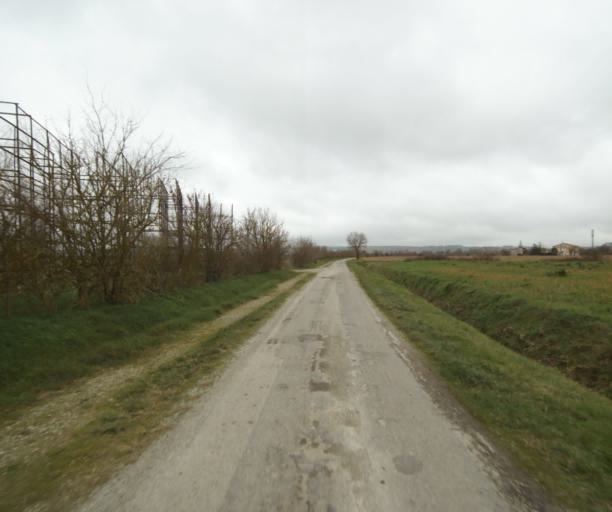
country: FR
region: Midi-Pyrenees
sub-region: Departement de l'Ariege
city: Mazeres
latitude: 43.2487
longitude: 1.6580
